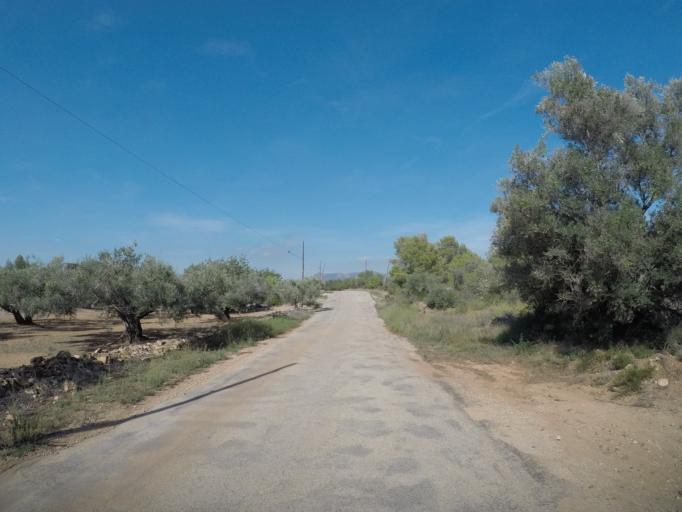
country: ES
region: Catalonia
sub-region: Provincia de Tarragona
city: El Perello
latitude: 40.8979
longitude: 0.7309
